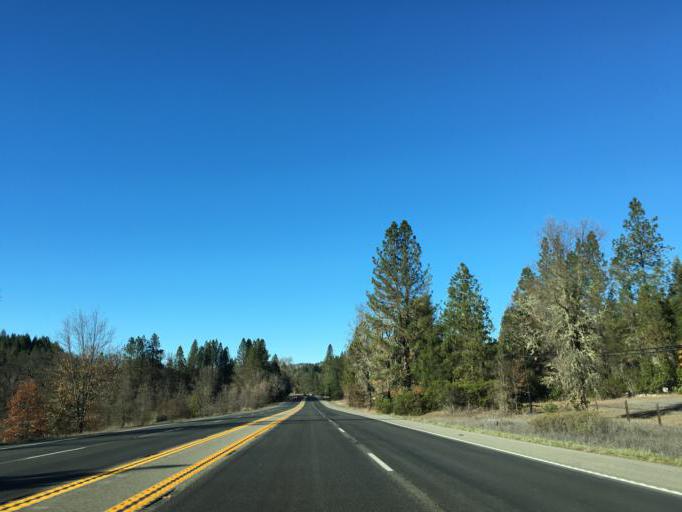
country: US
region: California
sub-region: Mendocino County
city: Laytonville
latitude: 39.7223
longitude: -123.5022
